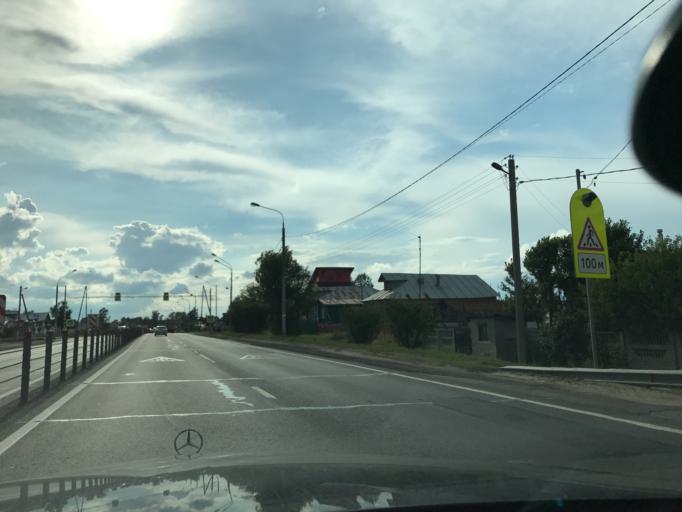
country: RU
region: Moskovskaya
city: Demikhovo
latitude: 55.8559
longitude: 38.8779
